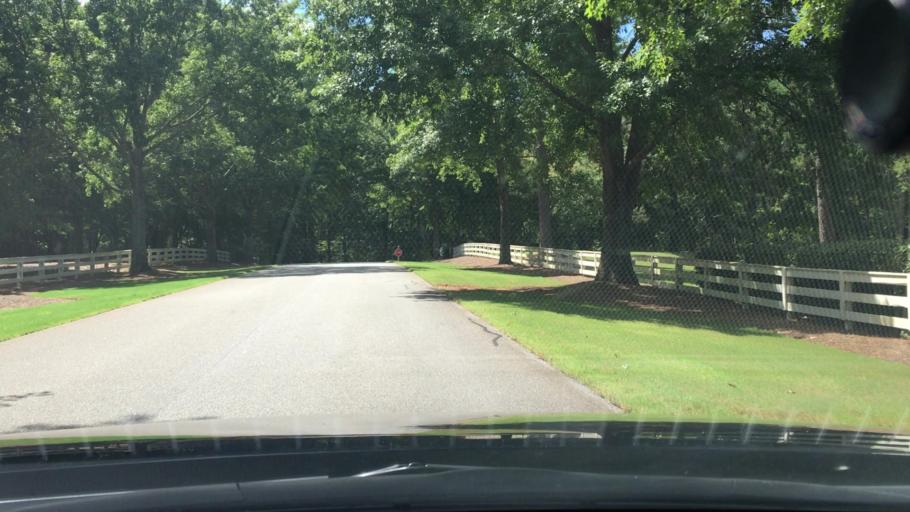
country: US
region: Georgia
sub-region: Putnam County
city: Jefferson
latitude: 33.3940
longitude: -83.2336
